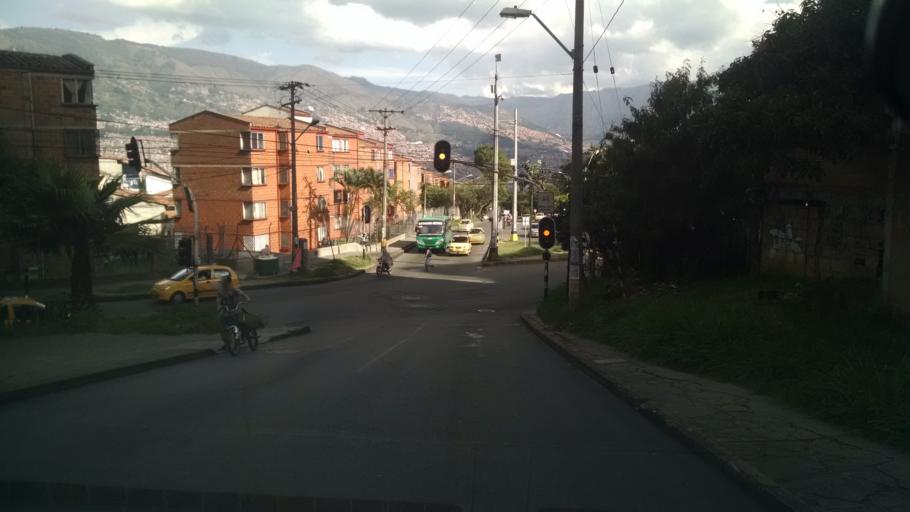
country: CO
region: Antioquia
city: Medellin
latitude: 6.2847
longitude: -75.5845
